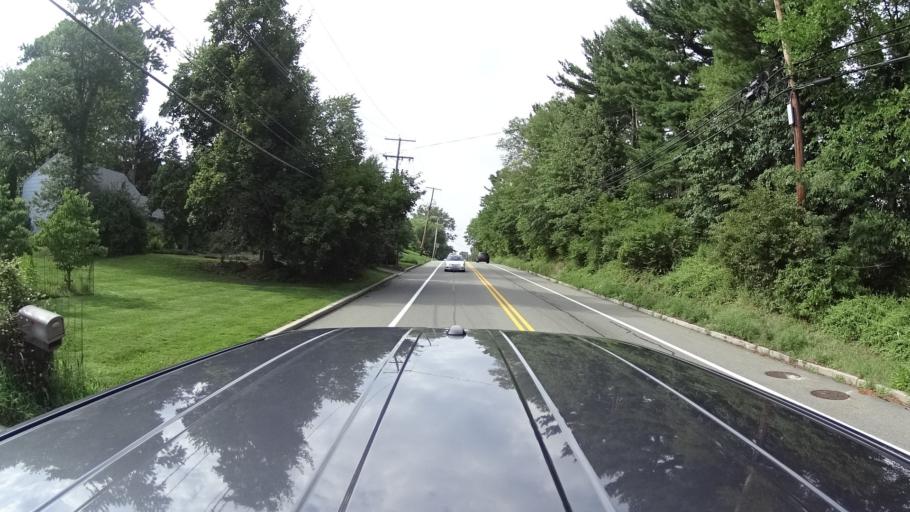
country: US
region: New Jersey
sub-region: Somerset County
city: Warren Township
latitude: 40.6566
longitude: -74.5298
